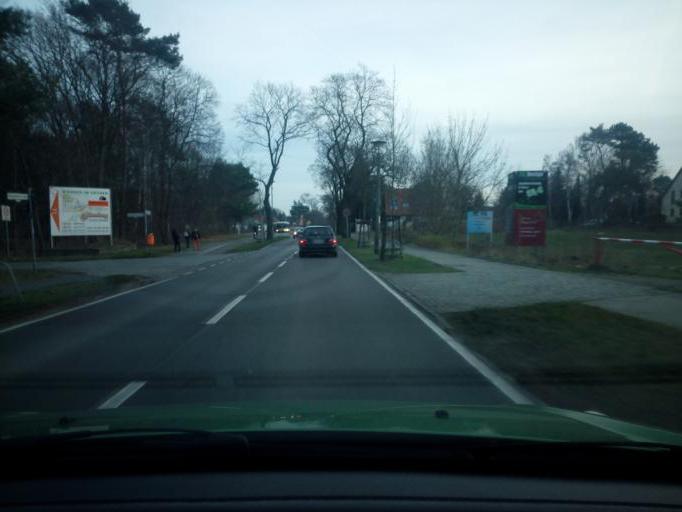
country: DE
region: Berlin
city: Muggelheim
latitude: 52.4162
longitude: 13.6547
